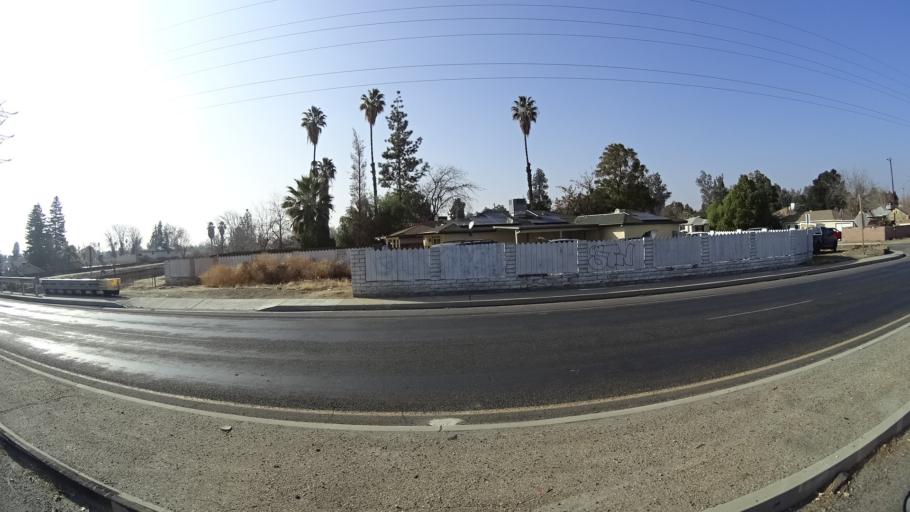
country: US
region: California
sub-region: Kern County
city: Oildale
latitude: 35.4160
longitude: -119.0127
